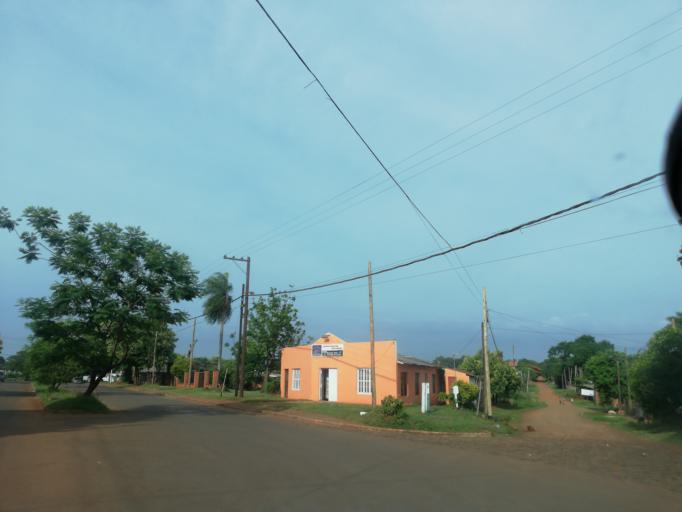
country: AR
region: Misiones
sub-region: Departamento de Capital
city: Posadas
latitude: -27.4110
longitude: -55.9153
